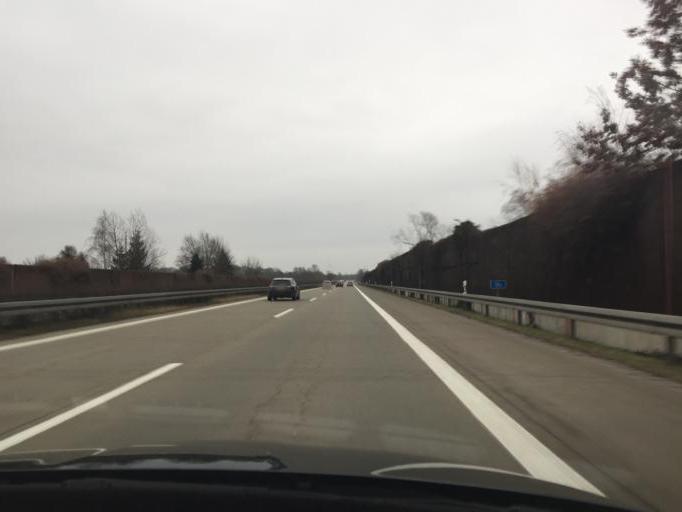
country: DE
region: Brandenburg
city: Vetschau
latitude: 51.8001
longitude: 14.0450
